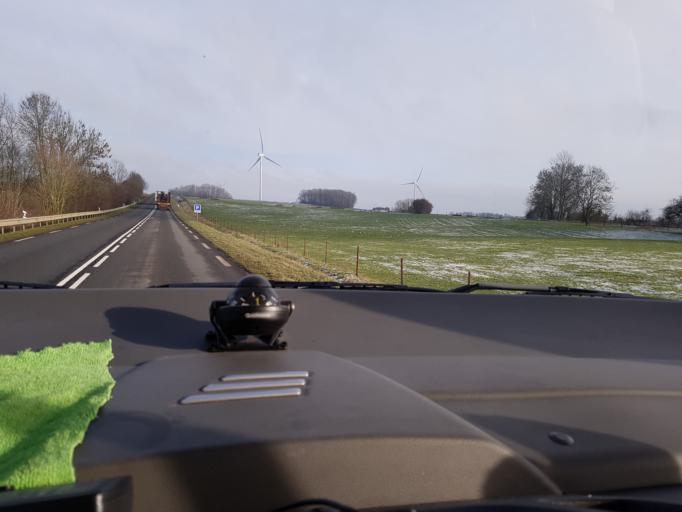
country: FR
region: Champagne-Ardenne
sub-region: Departement des Ardennes
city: Signy-le-Petit
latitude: 49.8622
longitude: 4.2750
